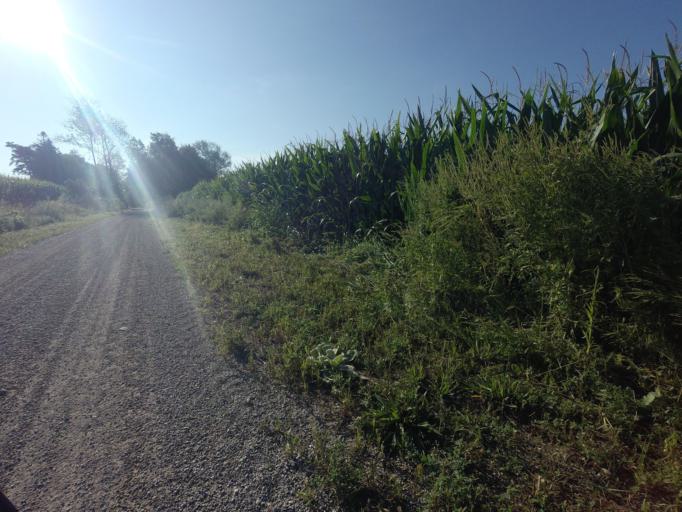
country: CA
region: Ontario
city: Goderich
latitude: 43.7443
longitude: -81.4909
